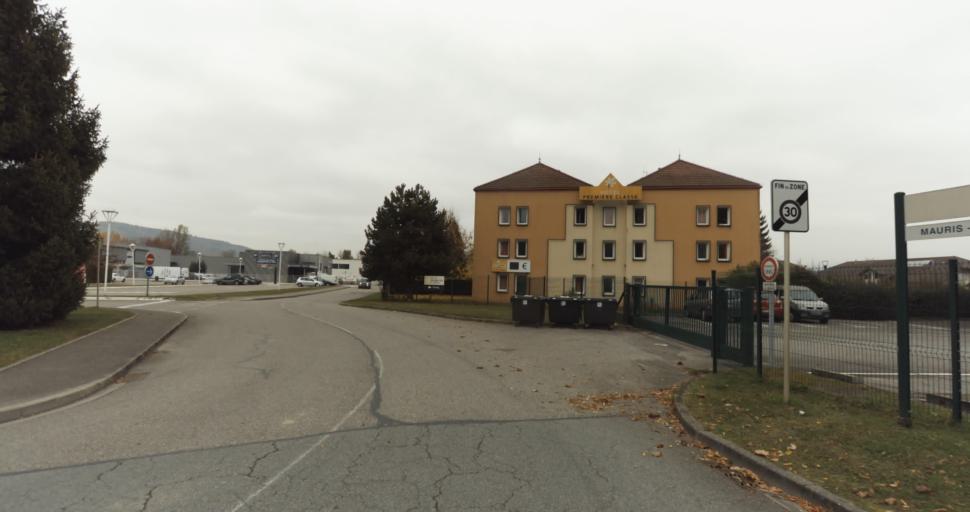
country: FR
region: Rhone-Alpes
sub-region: Departement de la Haute-Savoie
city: Epagny
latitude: 45.9288
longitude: 6.0837
